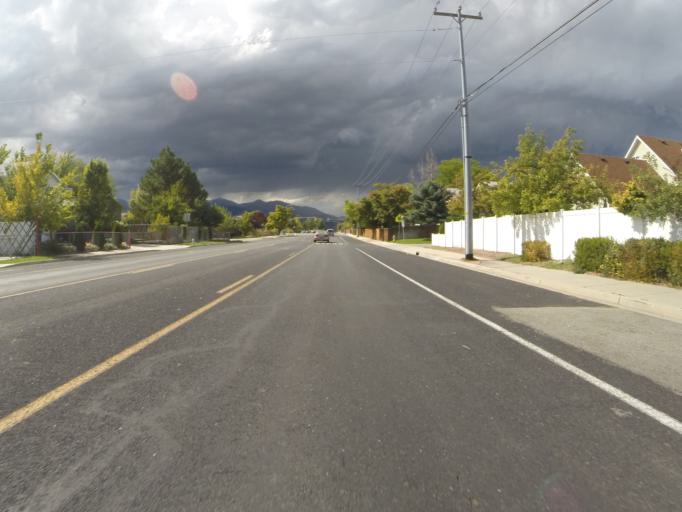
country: US
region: Utah
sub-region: Salt Lake County
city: West Valley City
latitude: 40.7039
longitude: -112.0038
